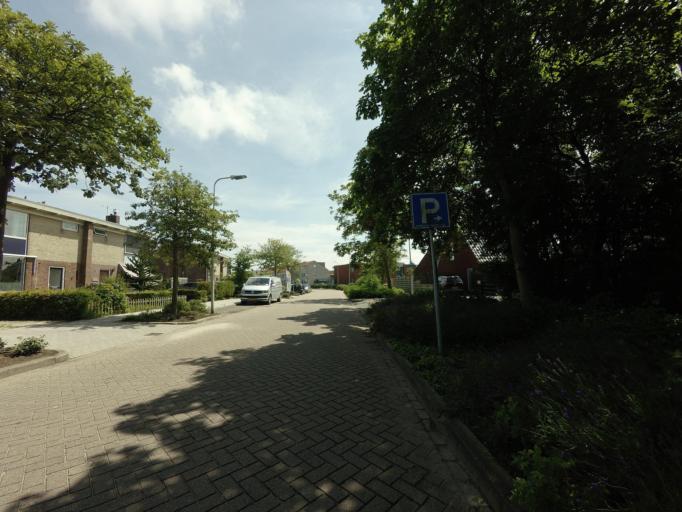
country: NL
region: North Holland
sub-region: Gemeente Texel
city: Den Burg
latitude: 53.0860
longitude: 4.8719
